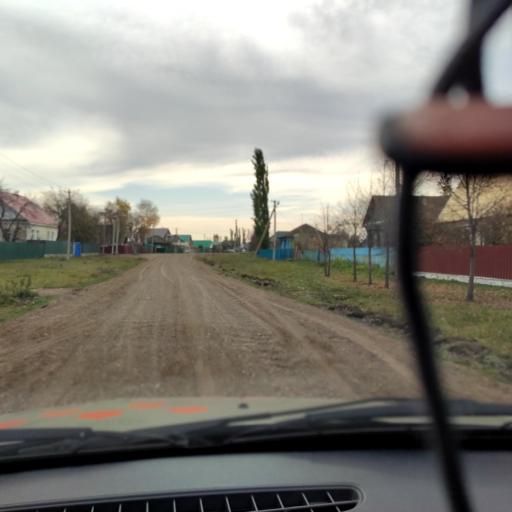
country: RU
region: Bashkortostan
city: Kabakovo
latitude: 54.5285
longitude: 56.0276
